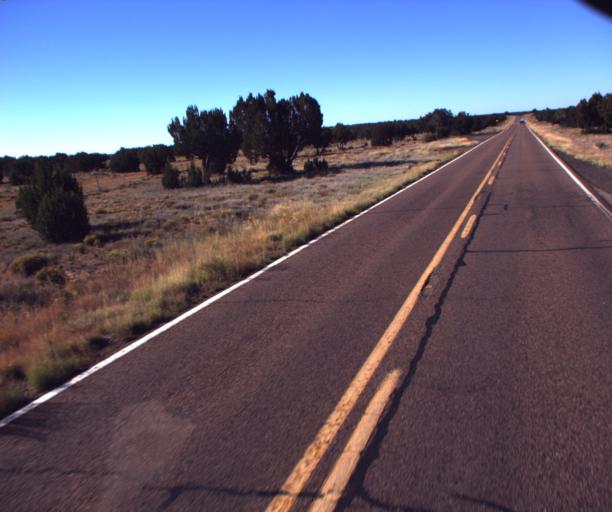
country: US
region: Arizona
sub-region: Navajo County
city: Heber-Overgaard
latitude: 34.5145
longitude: -110.4402
